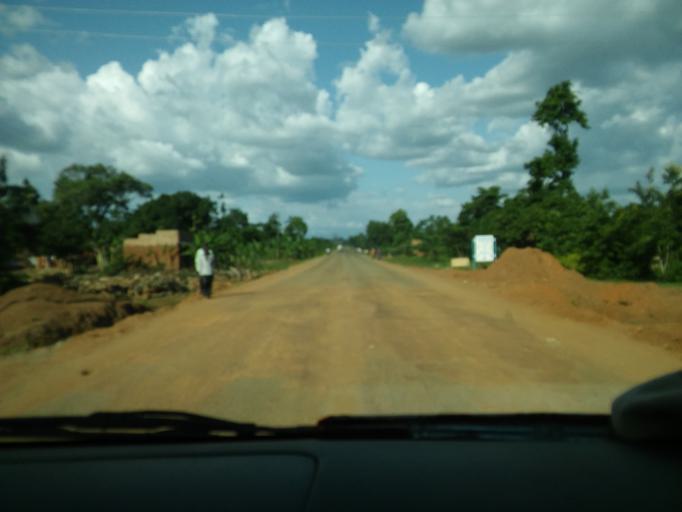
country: UG
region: Eastern Region
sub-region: Kibuku District
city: Kibuku
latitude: 1.0165
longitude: 33.8561
